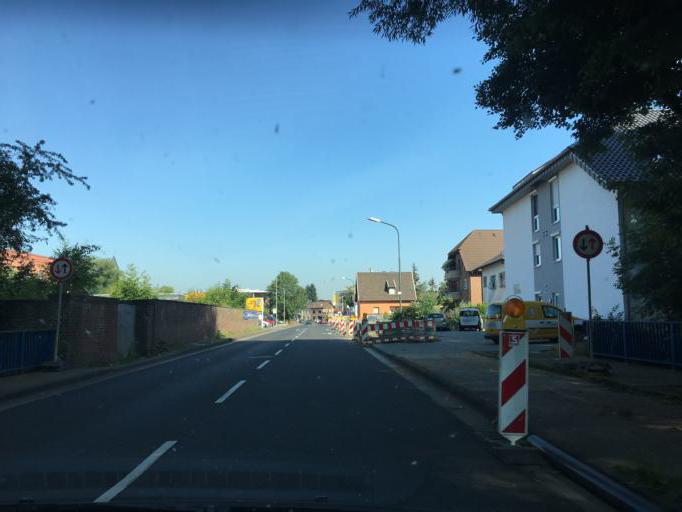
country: DE
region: North Rhine-Westphalia
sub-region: Regierungsbezirk Koln
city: Dueren
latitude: 50.8136
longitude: 6.4503
